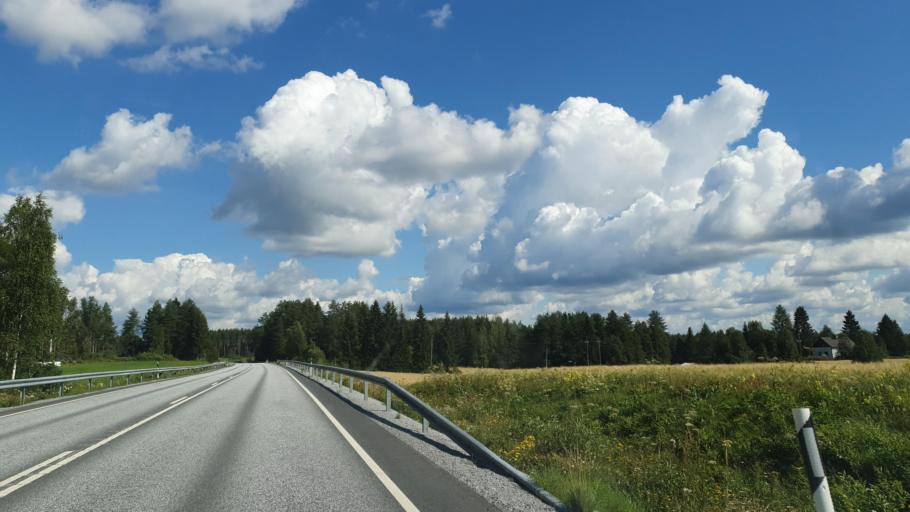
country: FI
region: Northern Savo
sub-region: Ylae-Savo
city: Sonkajaervi
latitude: 63.8408
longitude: 27.4305
